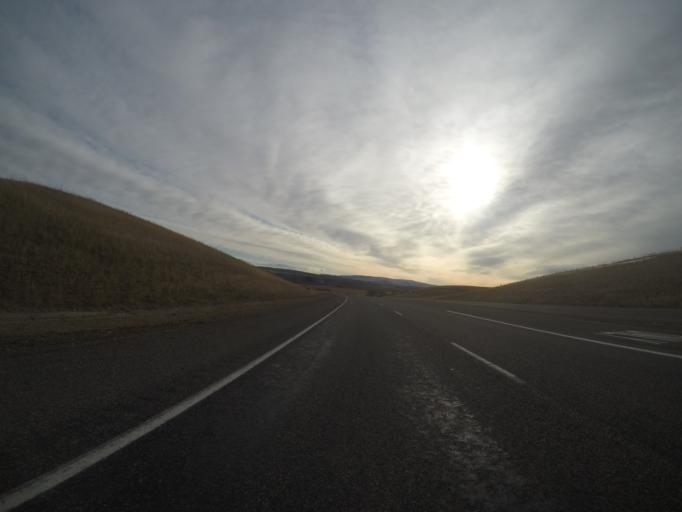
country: US
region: Montana
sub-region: Yellowstone County
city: Laurel
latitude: 45.5452
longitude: -108.8605
